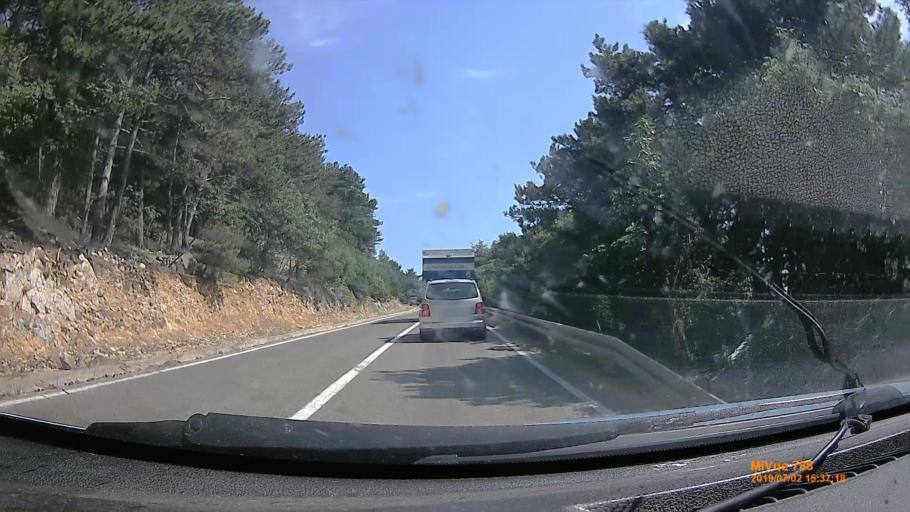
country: HR
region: Primorsko-Goranska
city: Cres
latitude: 44.9796
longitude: 14.4152
